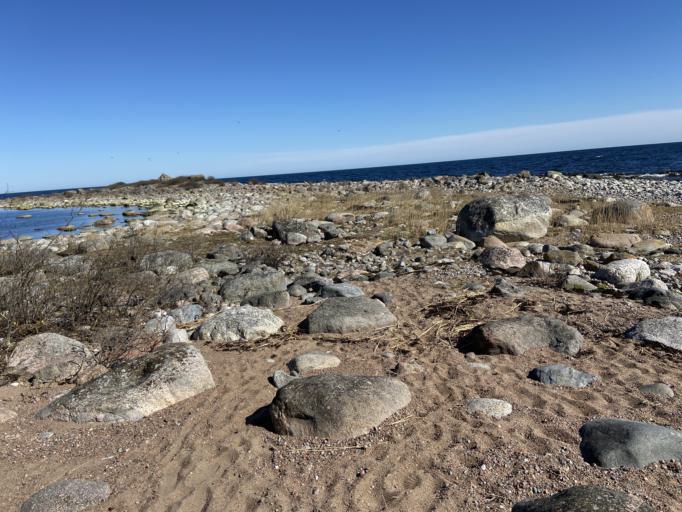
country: EE
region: Harju
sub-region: Loksa linn
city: Loksa
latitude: 59.6727
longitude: 25.6958
